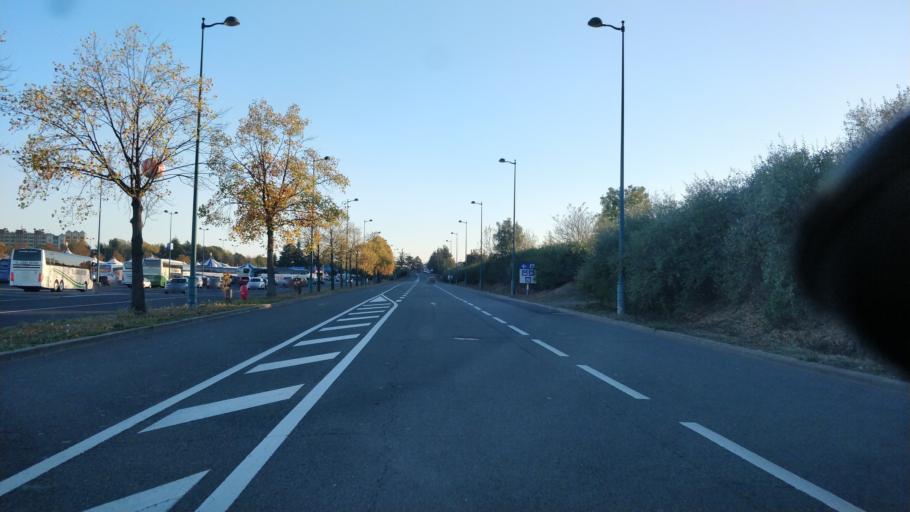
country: FR
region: Ile-de-France
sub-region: Departement de Seine-et-Marne
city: Chalifert
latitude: 48.8762
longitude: 2.7845
